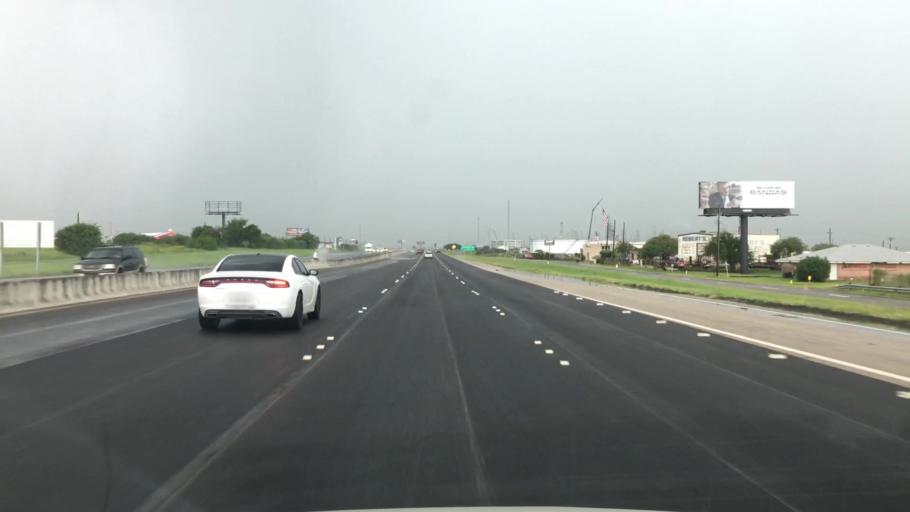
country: US
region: Texas
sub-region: Nueces County
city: Corpus Christi
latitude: 27.8141
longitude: -97.5082
